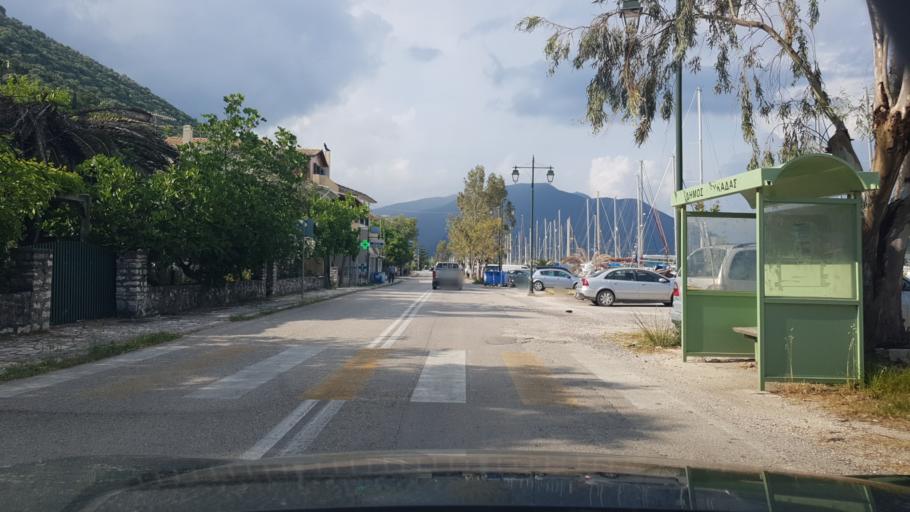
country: GR
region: Ionian Islands
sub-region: Lefkada
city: Nidri
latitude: 38.6824
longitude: 20.6983
